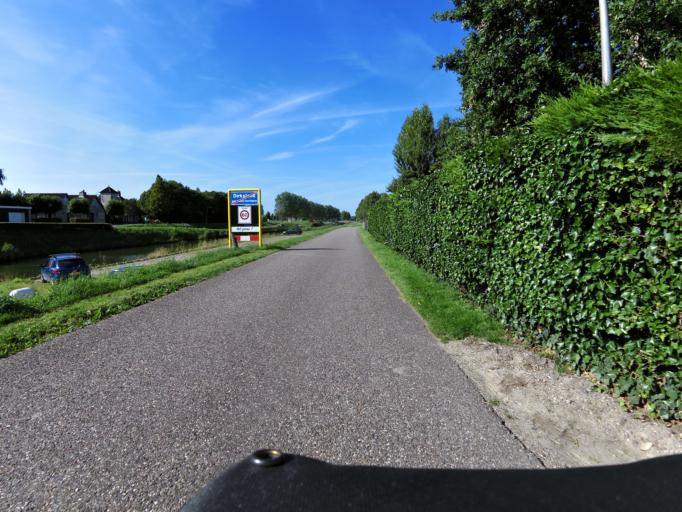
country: NL
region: South Holland
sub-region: Gemeente Goeree-Overflakkee
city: Dirksland
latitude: 51.7511
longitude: 4.1042
